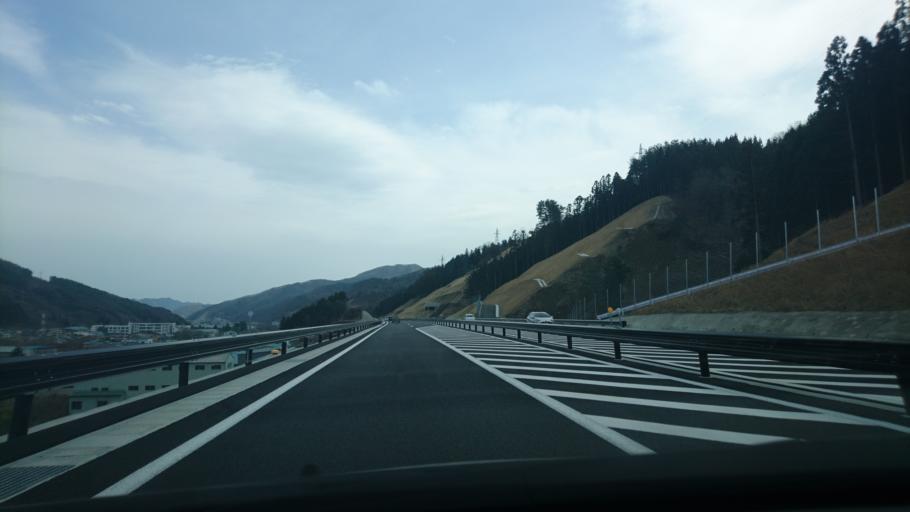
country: JP
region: Iwate
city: Kamaishi
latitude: 39.2511
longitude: 141.7960
